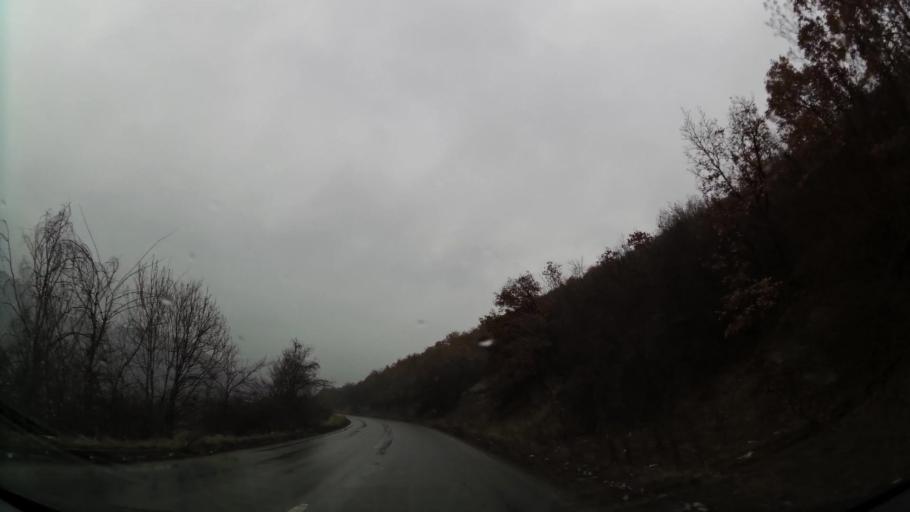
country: XK
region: Ferizaj
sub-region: Hani i Elezit
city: Hani i Elezit
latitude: 42.1324
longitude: 21.3117
